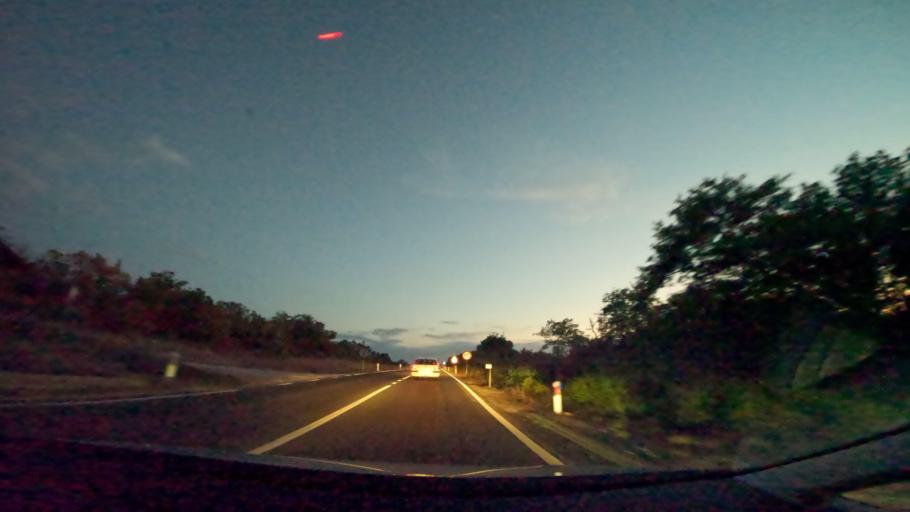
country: HR
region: Primorsko-Goranska
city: Njivice
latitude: 45.1603
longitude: 14.5508
